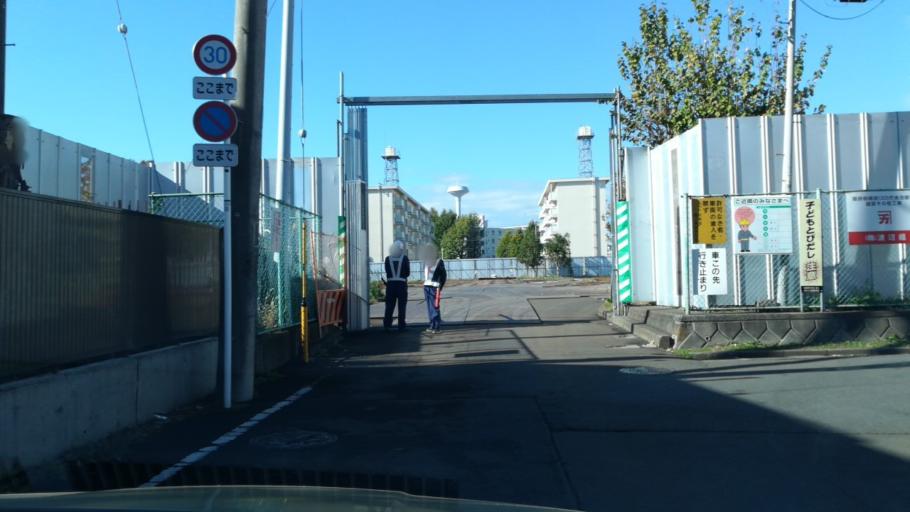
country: JP
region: Tokyo
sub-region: Machida-shi
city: Machida
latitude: 35.5769
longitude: 139.3905
